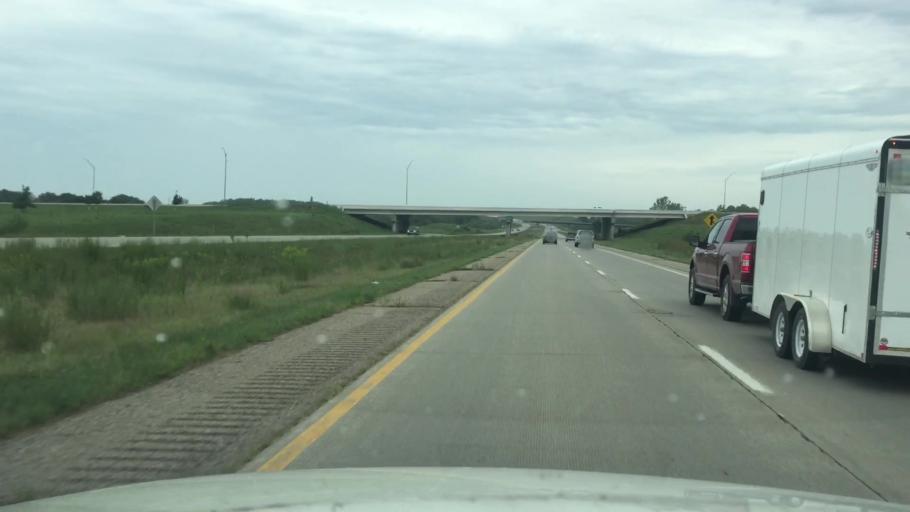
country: US
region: Iowa
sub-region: Warren County
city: Norwalk
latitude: 41.5064
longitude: -93.6421
